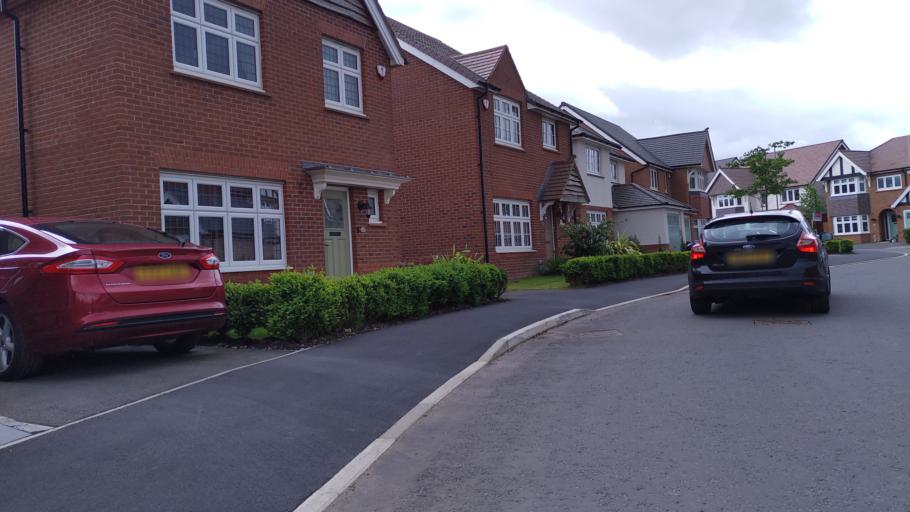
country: GB
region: England
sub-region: Lancashire
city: Euxton
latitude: 53.6753
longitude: -2.6670
